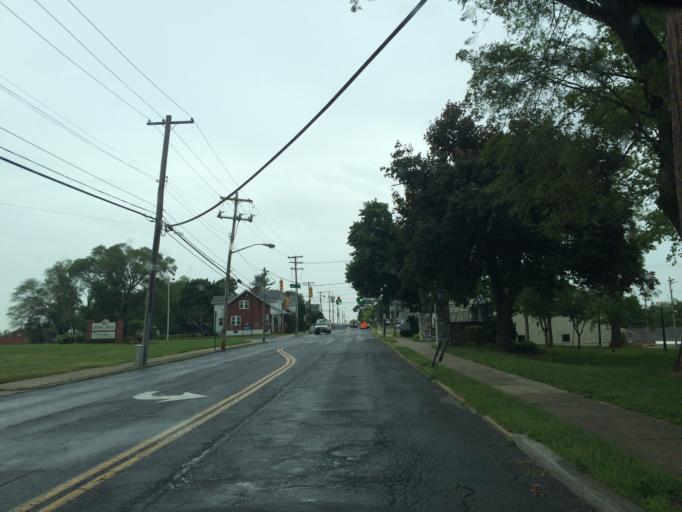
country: US
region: Maryland
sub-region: Washington County
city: Hagerstown
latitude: 39.6325
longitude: -77.7169
